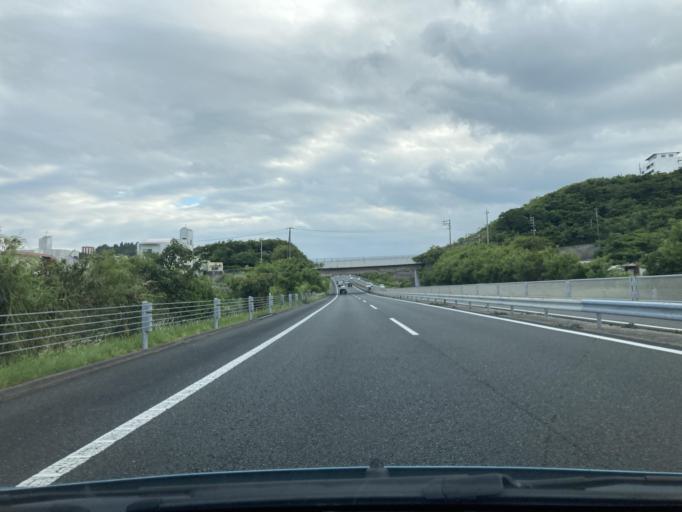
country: JP
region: Okinawa
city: Ginowan
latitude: 26.2359
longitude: 127.7406
